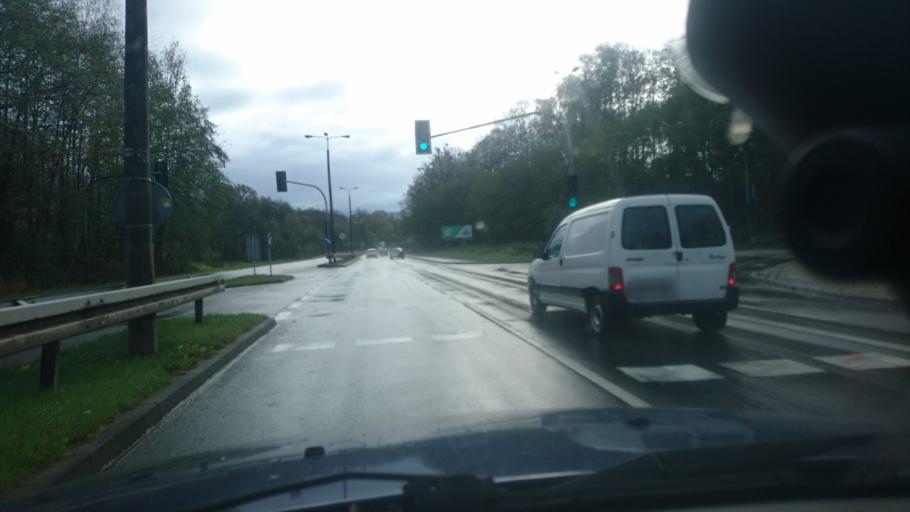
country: PL
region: Silesian Voivodeship
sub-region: Powiat bielski
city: Mazancowice
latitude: 49.8387
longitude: 19.0058
